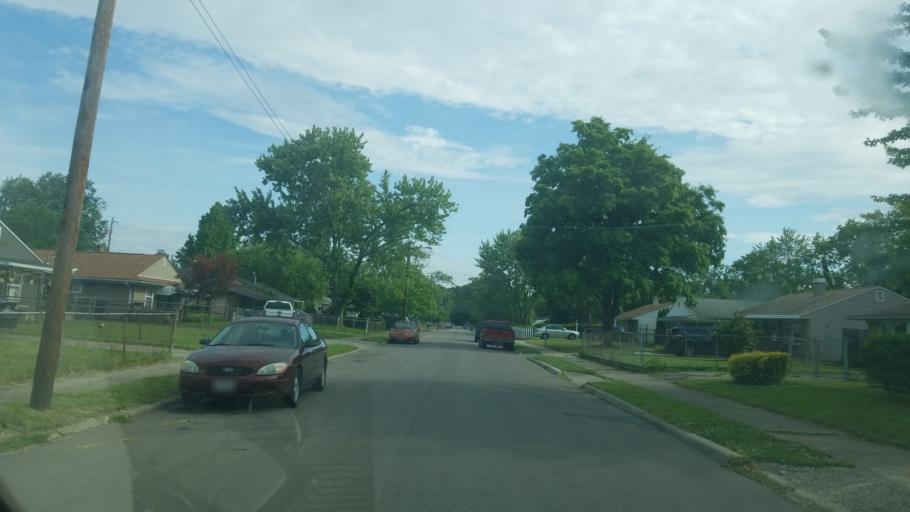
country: US
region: Ohio
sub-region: Franklin County
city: Minerva Park
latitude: 40.0375
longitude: -82.9736
